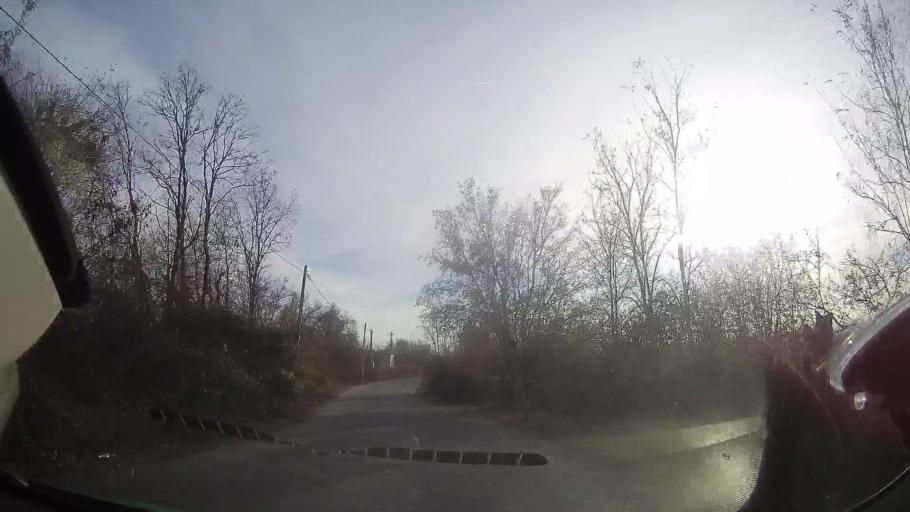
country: RO
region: Bihor
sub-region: Comuna Sarbi
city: Burzuc
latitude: 47.1175
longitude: 22.1790
